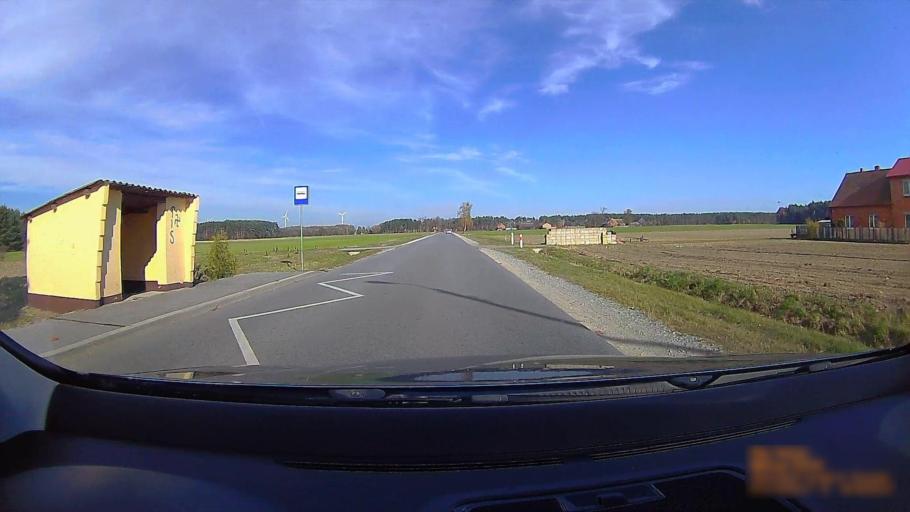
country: PL
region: Greater Poland Voivodeship
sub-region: Powiat ostrzeszowski
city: Doruchow
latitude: 51.3795
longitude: 18.0427
